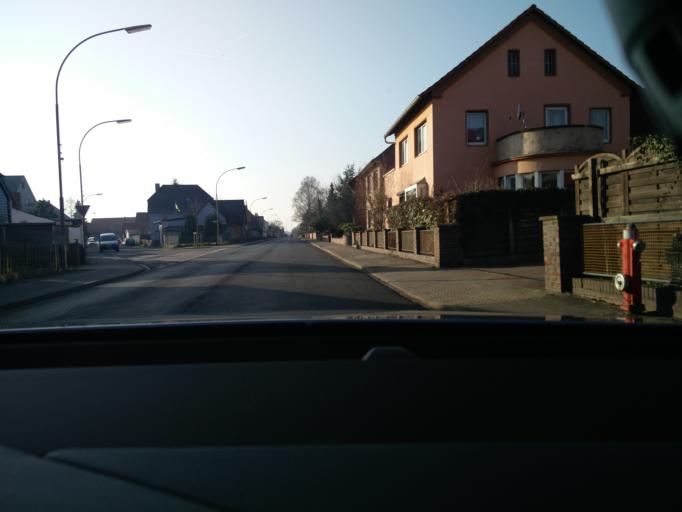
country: DE
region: Lower Saxony
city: Peine
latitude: 52.3421
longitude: 10.1785
